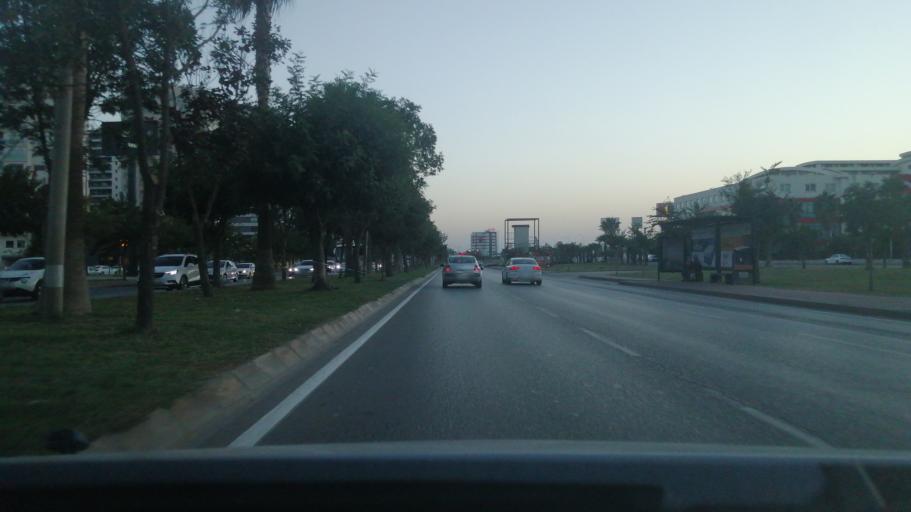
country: TR
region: Adana
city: Seyhan
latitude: 37.0202
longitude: 35.2526
